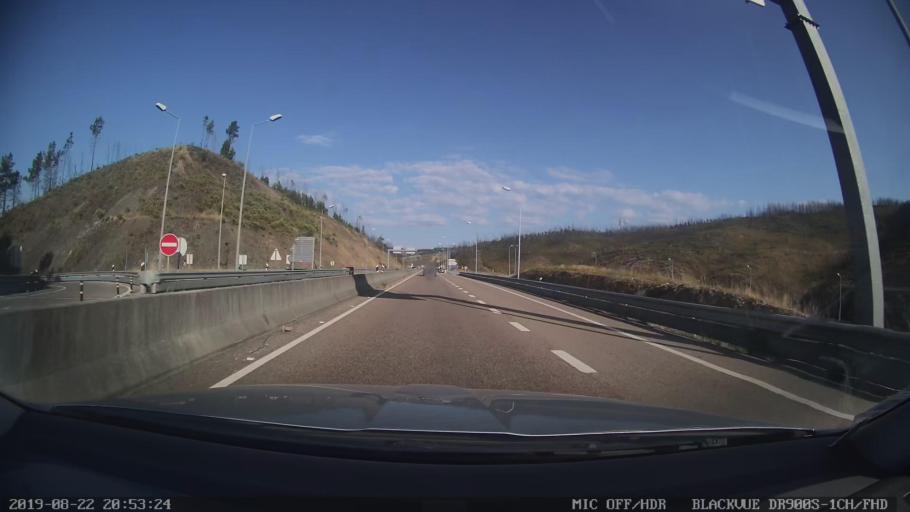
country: PT
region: Castelo Branco
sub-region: Proenca-A-Nova
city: Proenca-a-Nova
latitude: 39.7699
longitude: -7.9913
